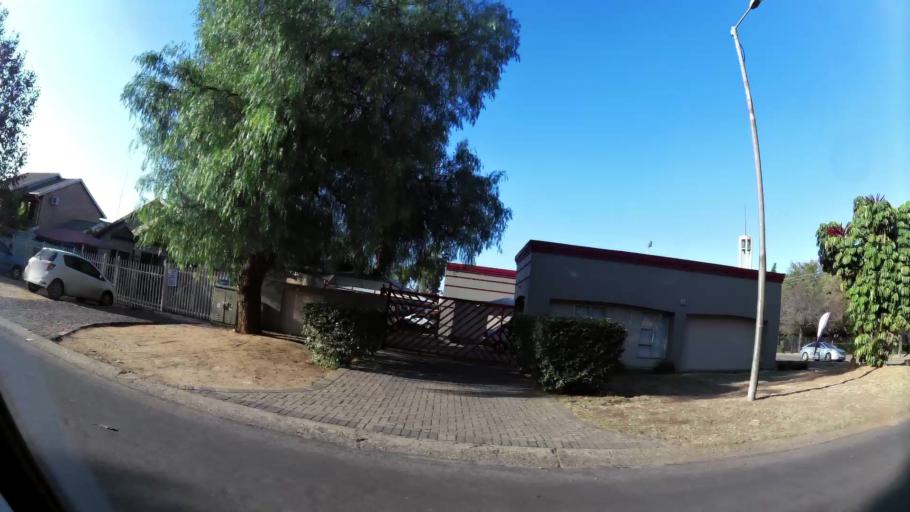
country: ZA
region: North-West
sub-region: Bojanala Platinum District Municipality
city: Rustenburg
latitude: -25.6799
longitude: 27.2360
